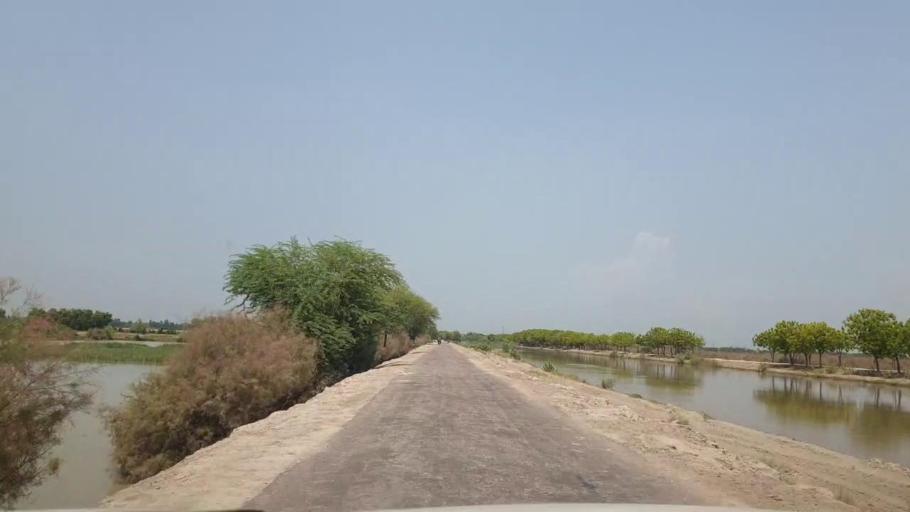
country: PK
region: Sindh
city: Dokri
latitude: 27.3505
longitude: 68.1123
